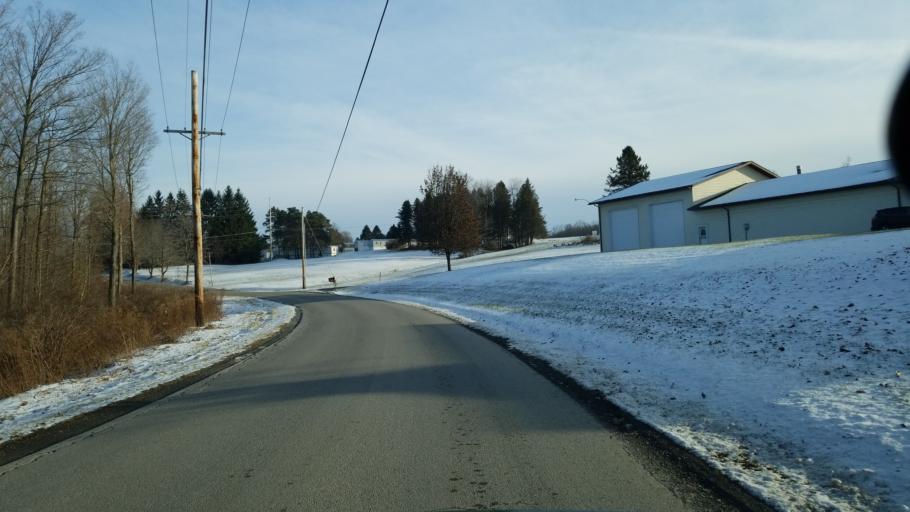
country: US
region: Pennsylvania
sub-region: Clearfield County
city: DuBois
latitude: 41.1130
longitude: -78.7051
